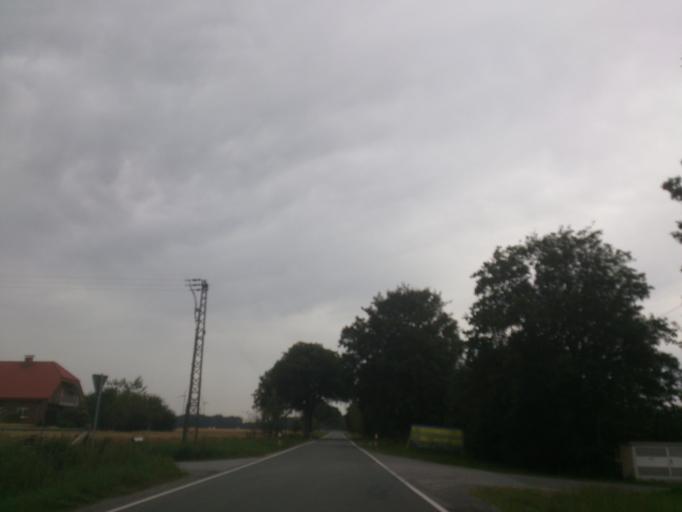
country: DE
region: North Rhine-Westphalia
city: Lichtenau
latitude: 51.5560
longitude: 8.8309
